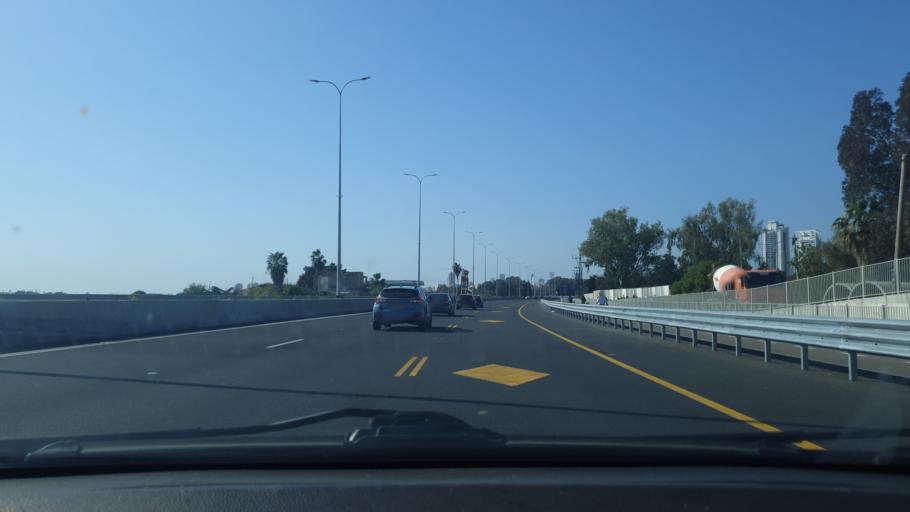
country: IL
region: Tel Aviv
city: Azor
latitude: 32.0391
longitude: 34.8257
